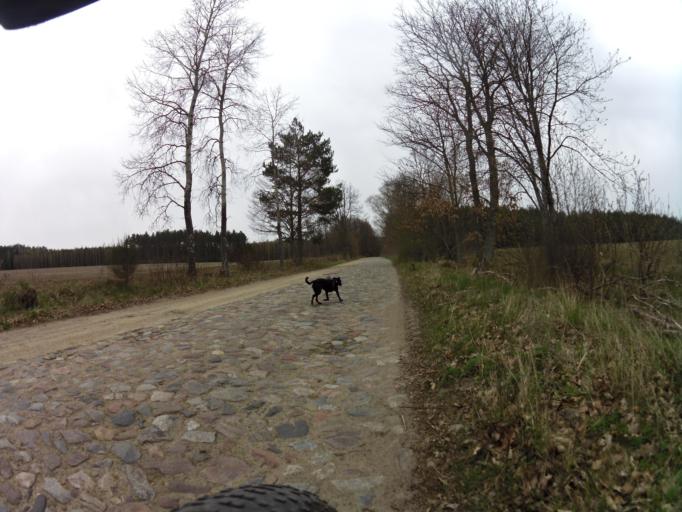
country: PL
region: West Pomeranian Voivodeship
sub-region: Powiat koszalinski
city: Bobolice
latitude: 54.0377
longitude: 16.6129
